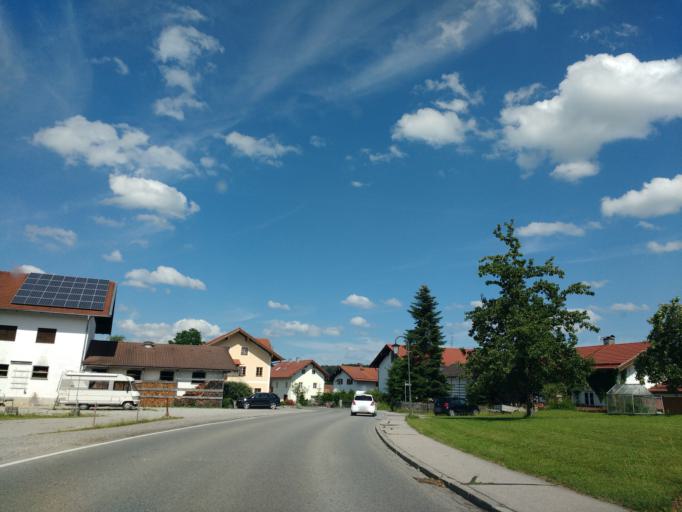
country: DE
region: Bavaria
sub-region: Upper Bavaria
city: Halfing
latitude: 47.9494
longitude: 12.2705
